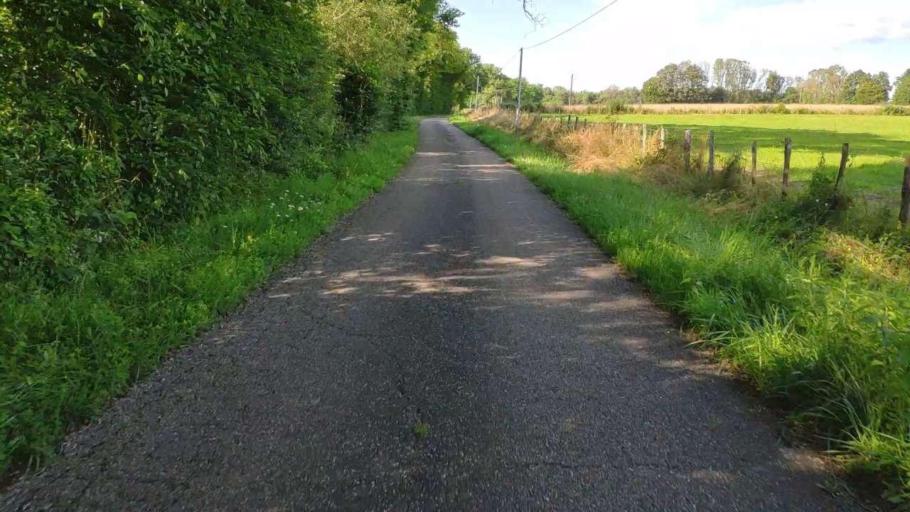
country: FR
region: Franche-Comte
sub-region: Departement du Jura
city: Bletterans
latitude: 46.8237
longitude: 5.5006
